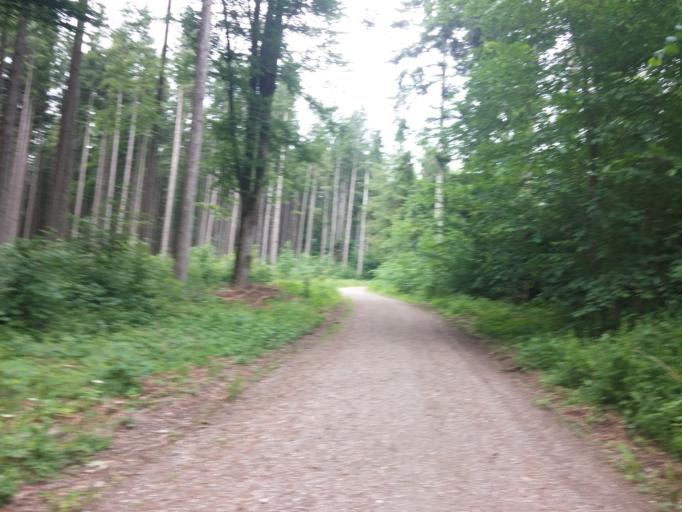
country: DE
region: Bavaria
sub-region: Swabia
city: Lautrach
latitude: 47.8916
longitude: 10.1053
